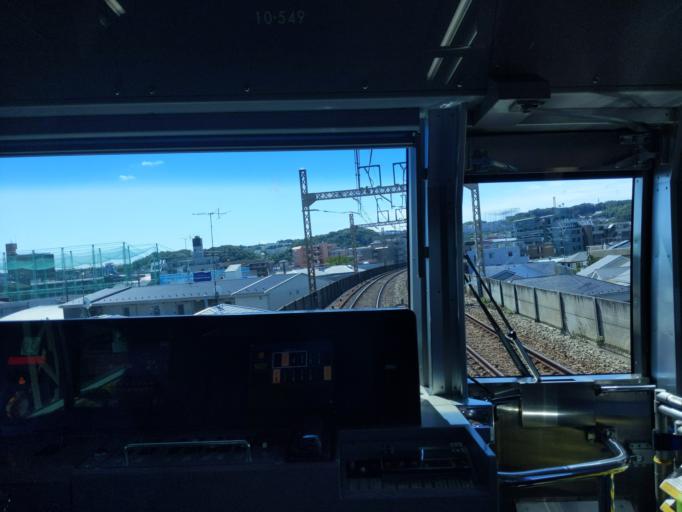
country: JP
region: Tokyo
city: Chofugaoka
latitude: 35.6381
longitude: 139.5350
